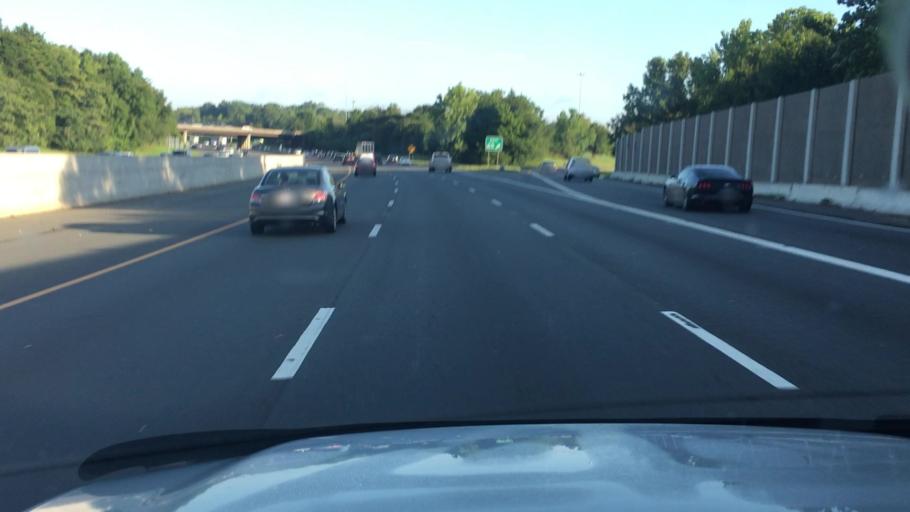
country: US
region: North Carolina
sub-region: Mecklenburg County
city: Pineville
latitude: 35.0991
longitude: -80.8777
